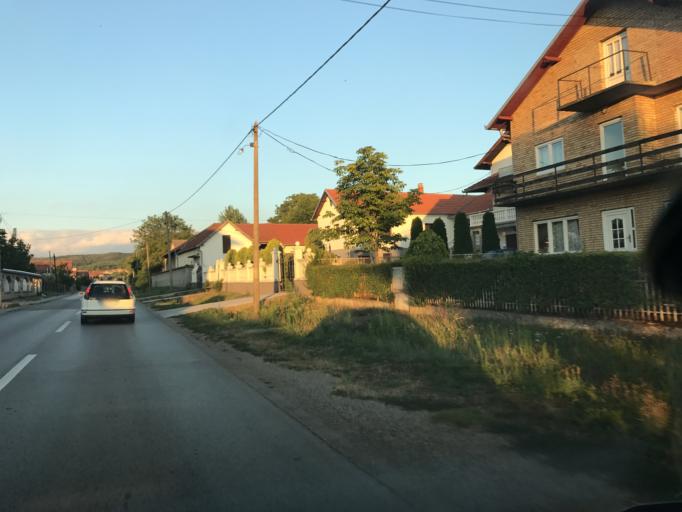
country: RS
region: Central Serbia
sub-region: Branicevski Okrug
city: Veliko Gradiste
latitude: 44.7203
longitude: 21.4327
